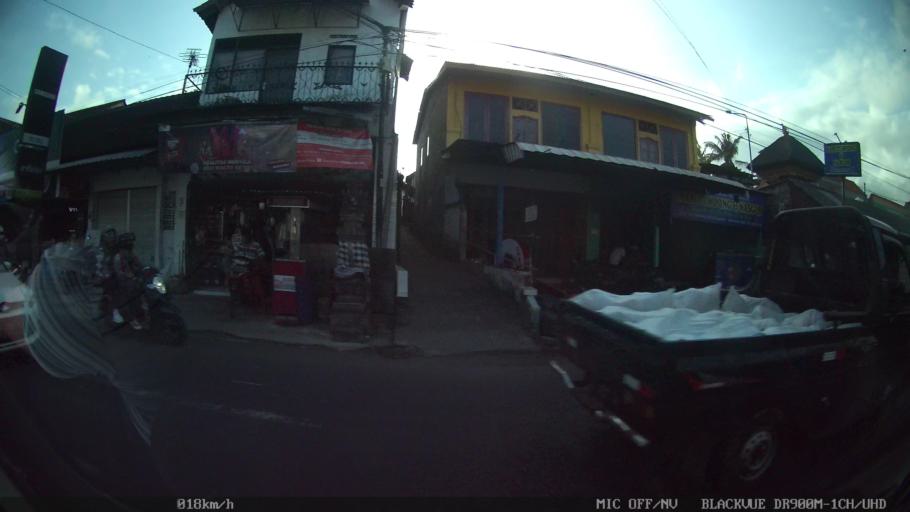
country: ID
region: Bali
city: Banjar Batur
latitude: -8.6063
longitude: 115.2136
